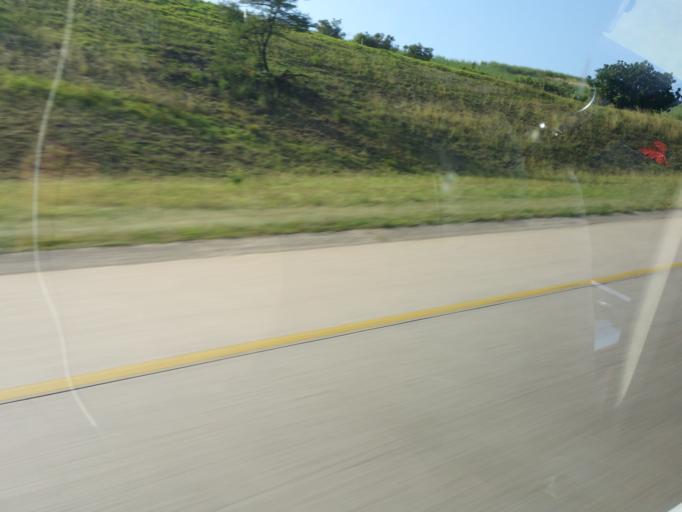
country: ZA
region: KwaZulu-Natal
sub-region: iLembe District Municipality
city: Stanger
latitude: -29.3835
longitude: 31.2971
